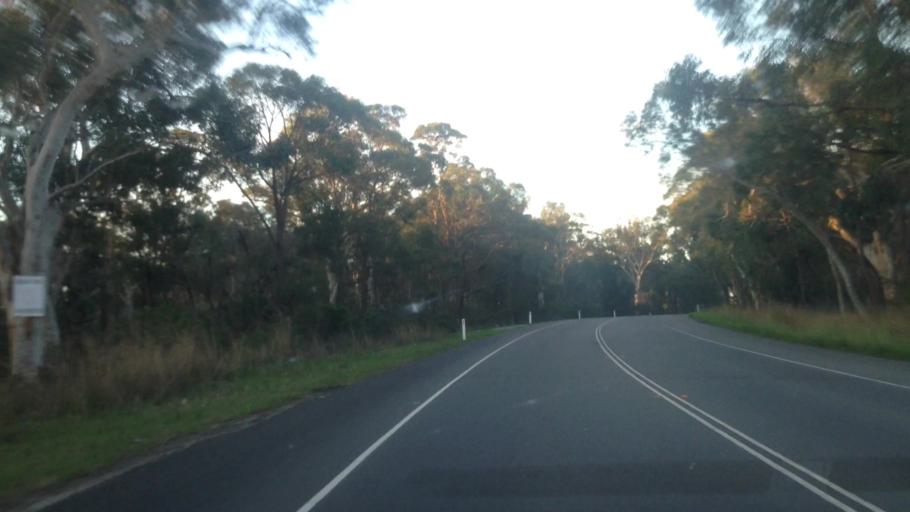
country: AU
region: New South Wales
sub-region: Lake Macquarie Shire
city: Dora Creek
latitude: -33.1244
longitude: 151.4753
